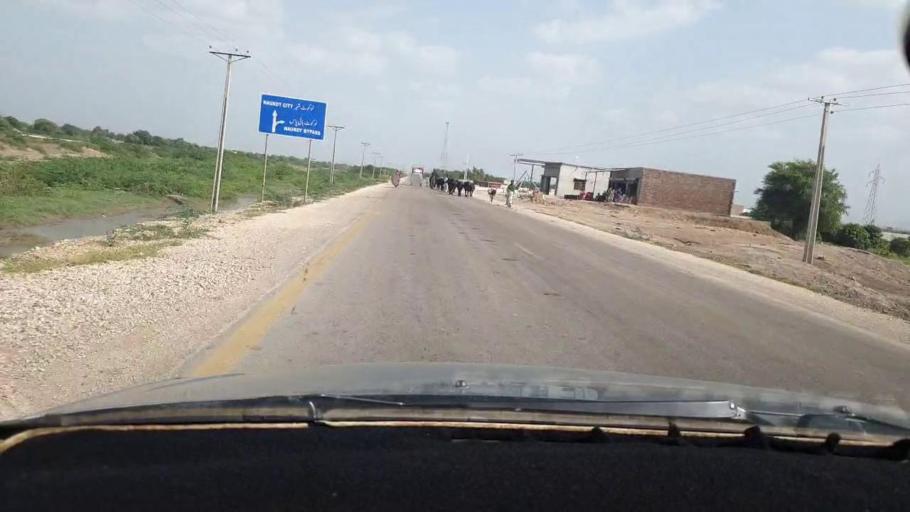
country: PK
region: Sindh
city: Naukot
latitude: 24.8680
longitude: 69.3802
